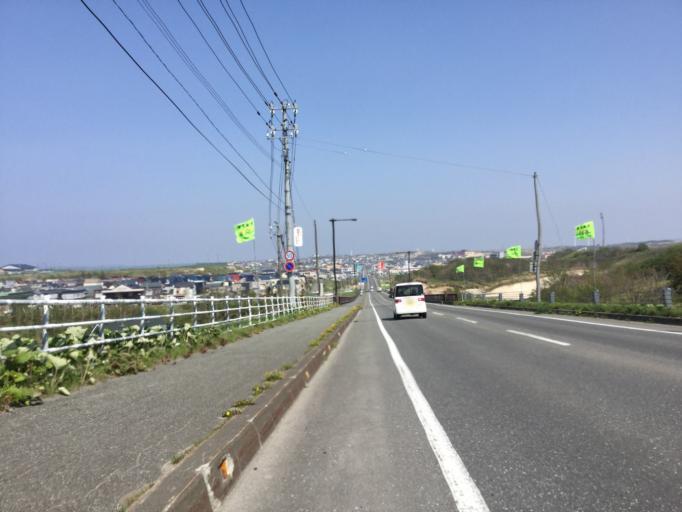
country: JP
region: Hokkaido
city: Wakkanai
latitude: 45.3865
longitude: 141.6880
